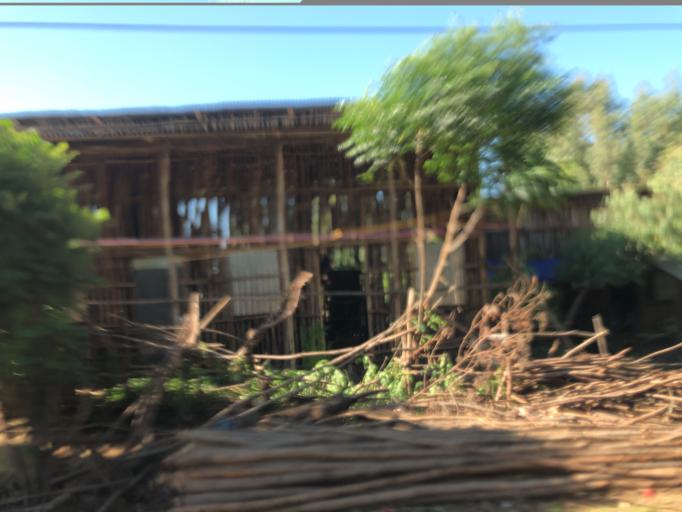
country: ET
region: Amhara
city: Gondar
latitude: 12.4760
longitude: 37.4809
